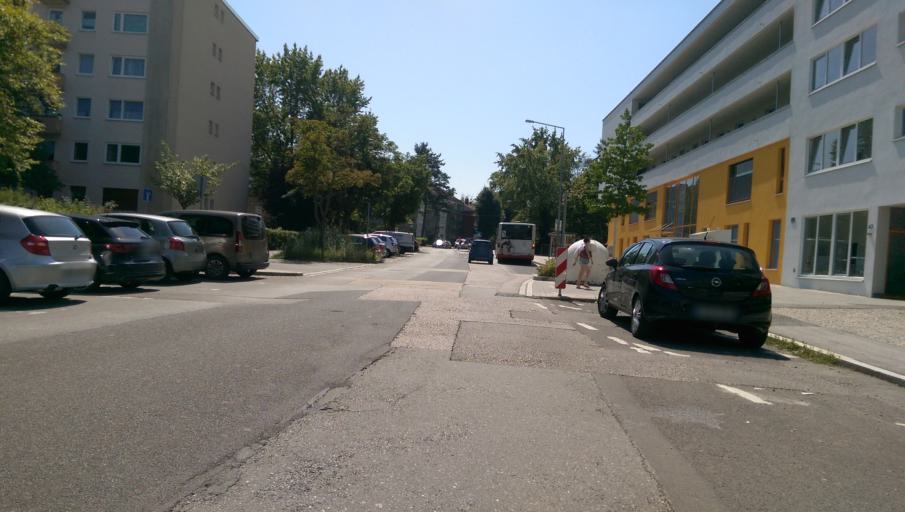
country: DE
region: Bavaria
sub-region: Regierungsbezirk Mittelfranken
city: Nuernberg
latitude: 49.4686
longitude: 11.1032
